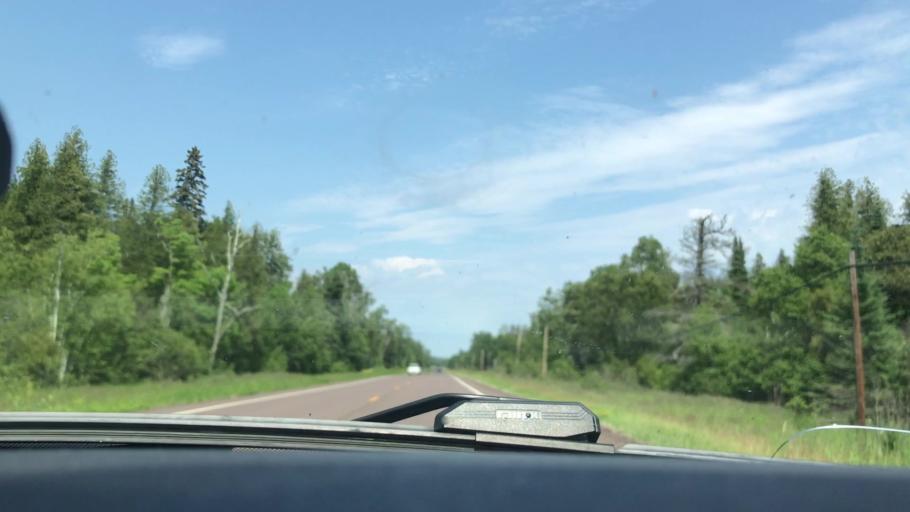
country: US
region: Minnesota
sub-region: Cook County
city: Grand Marais
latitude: 47.6310
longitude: -90.7255
